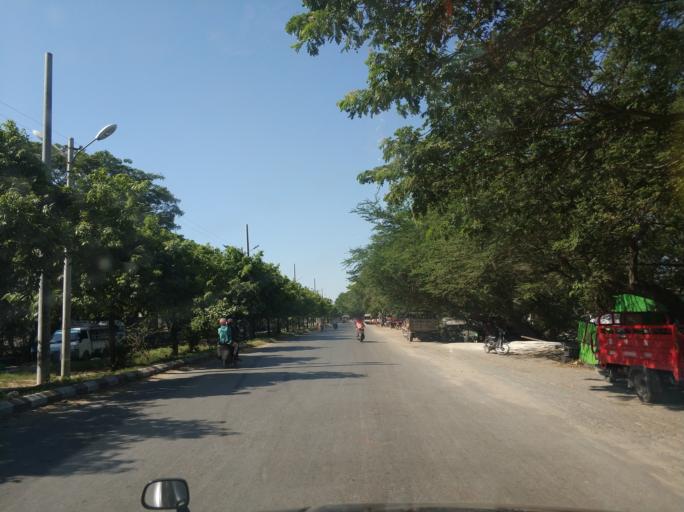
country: MM
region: Mandalay
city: Mandalay
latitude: 21.9663
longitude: 96.0561
